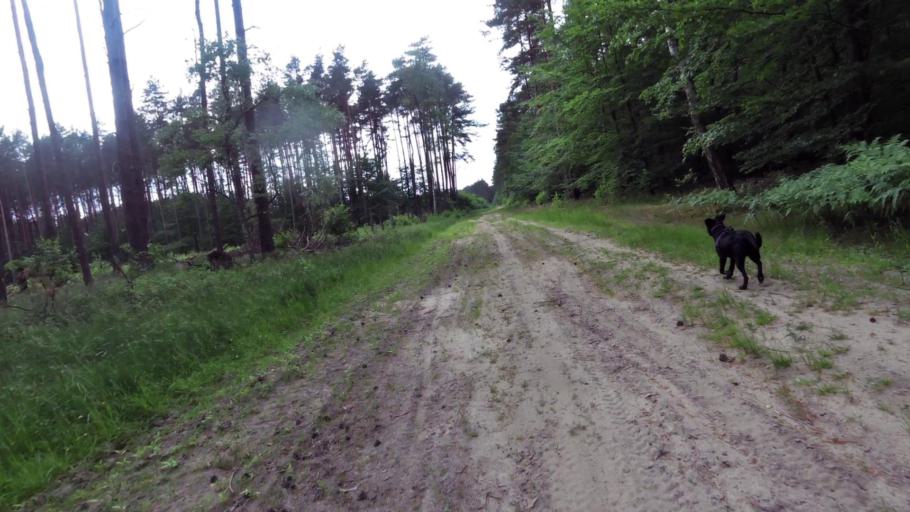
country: PL
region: West Pomeranian Voivodeship
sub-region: Powiat mysliborski
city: Debno
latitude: 52.8375
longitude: 14.6254
